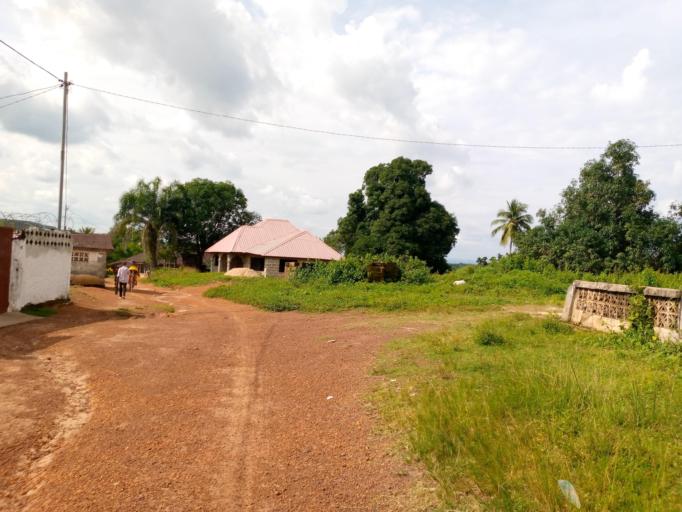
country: SL
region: Northern Province
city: Magburaka
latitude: 8.7272
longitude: -11.9473
